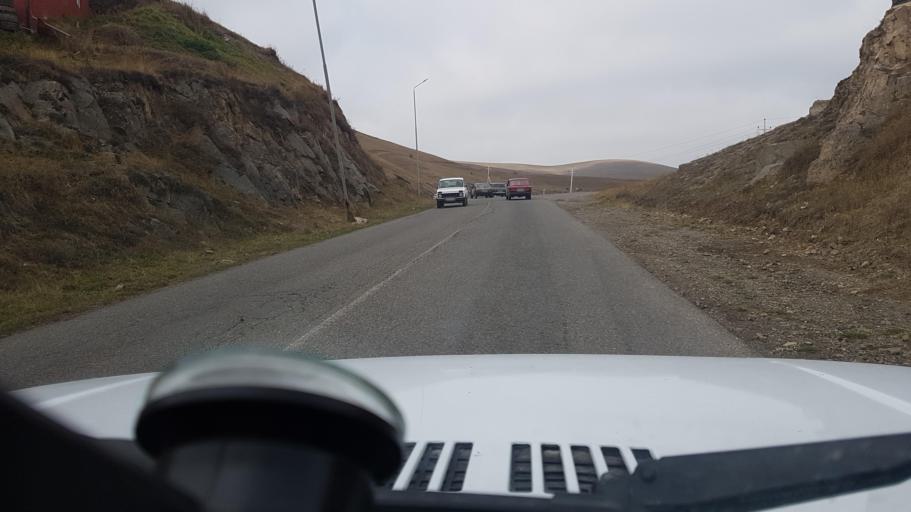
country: AZ
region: Gadabay Rayon
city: Ariqdam
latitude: 40.6136
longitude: 45.8121
